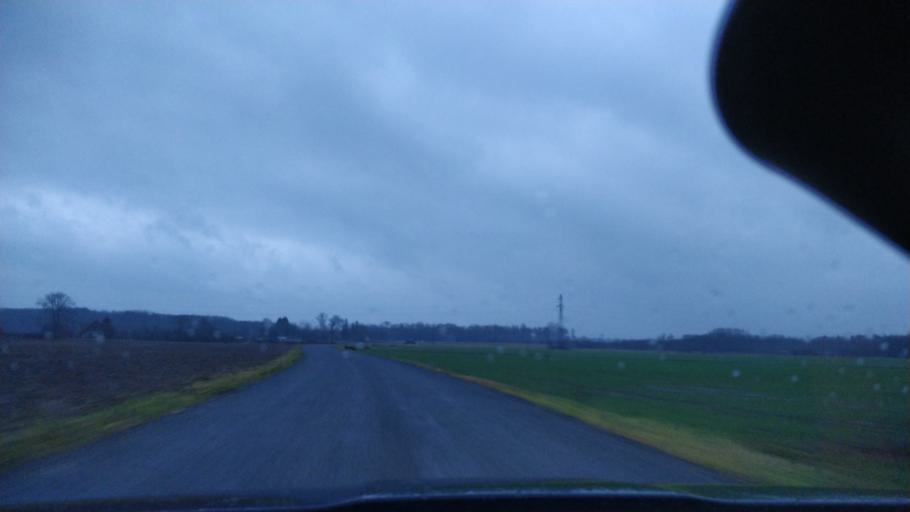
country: EE
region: Laeaene
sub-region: Lihula vald
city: Lihula
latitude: 58.8379
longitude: 24.0462
